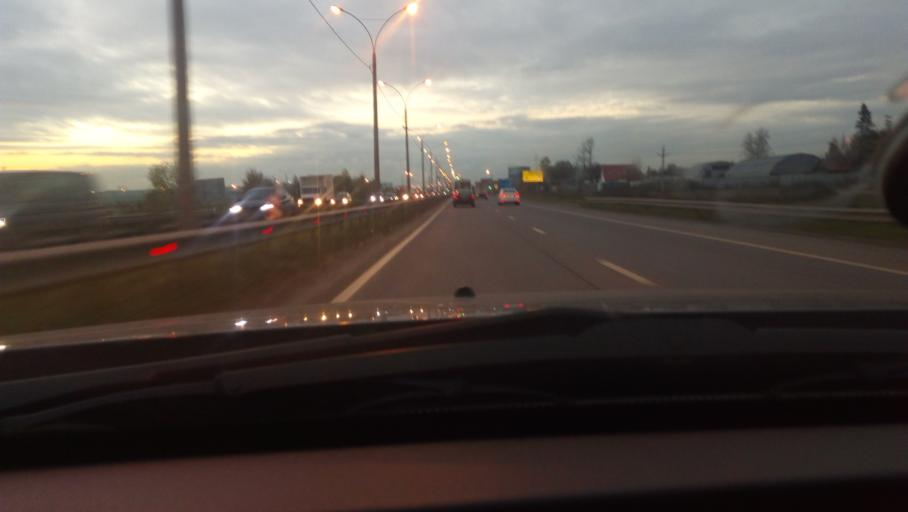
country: RU
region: Moskovskaya
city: Yam
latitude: 55.4669
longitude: 37.7514
